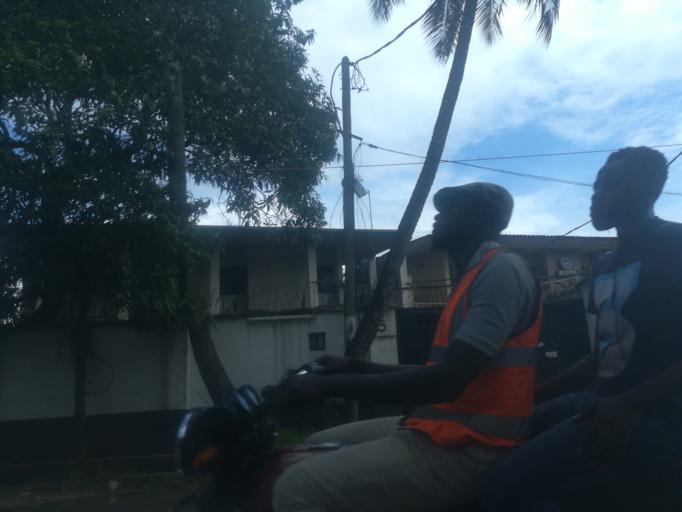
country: NG
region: Lagos
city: Somolu
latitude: 6.5502
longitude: 3.3751
